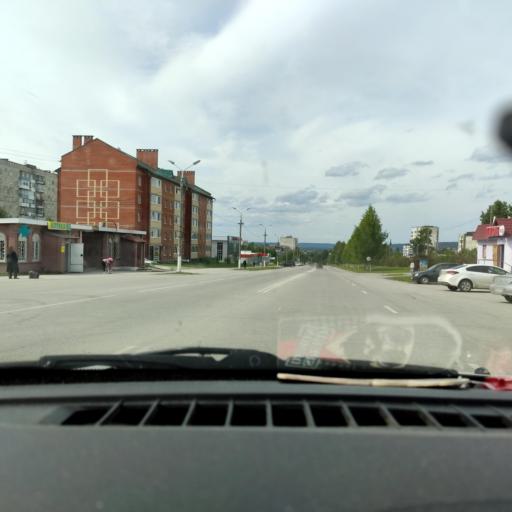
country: RU
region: Perm
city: Chusovoy
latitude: 58.2715
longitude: 57.8010
